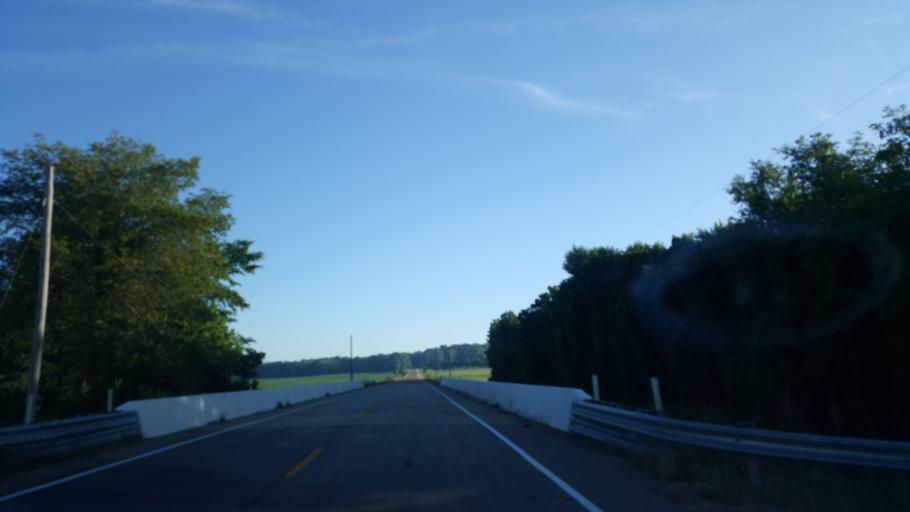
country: US
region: Tennessee
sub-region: McNairy County
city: Adamsville
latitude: 35.4363
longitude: -88.3720
